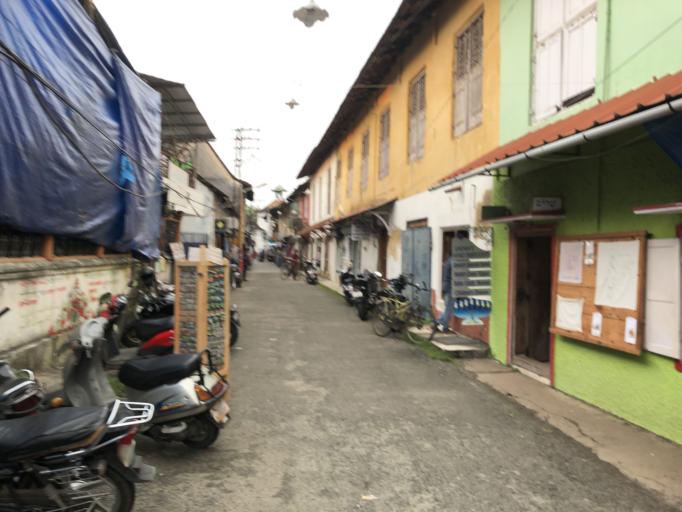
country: IN
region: Kerala
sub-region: Ernakulam
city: Cochin
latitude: 9.9566
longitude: 76.2599
